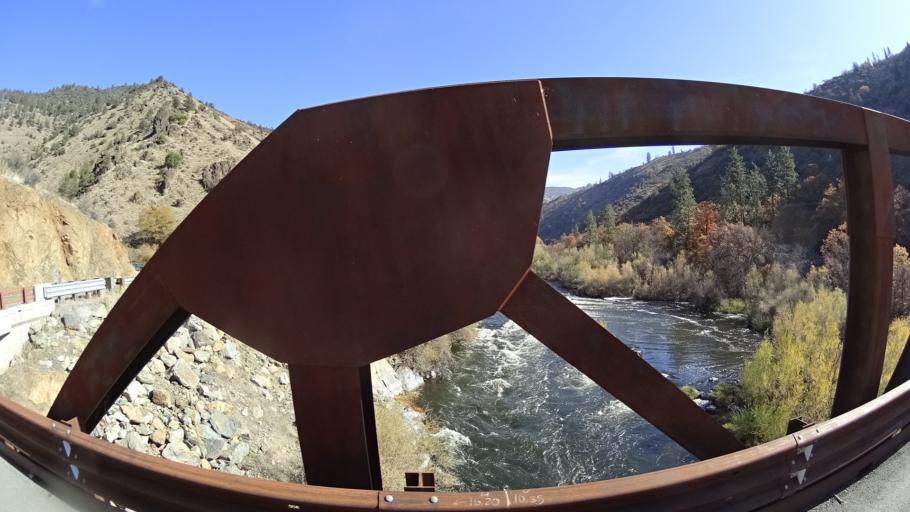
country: US
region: California
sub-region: Siskiyou County
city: Yreka
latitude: 41.8337
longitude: -122.6206
